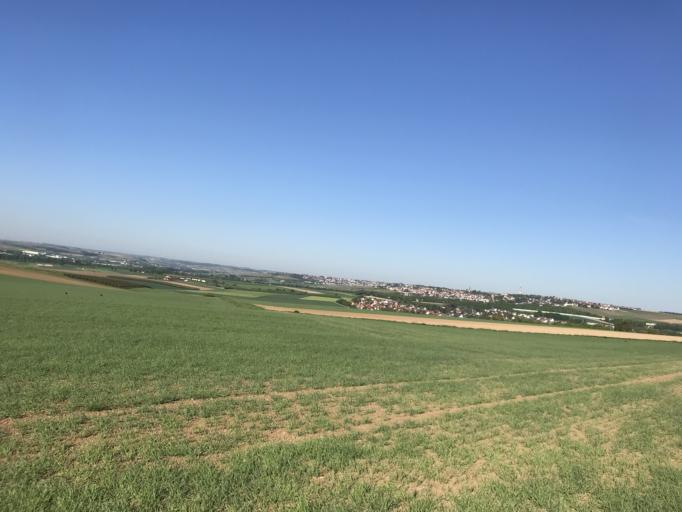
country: DE
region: Rheinland-Pfalz
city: Klein-Winternheim
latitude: 49.9365
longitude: 8.2314
